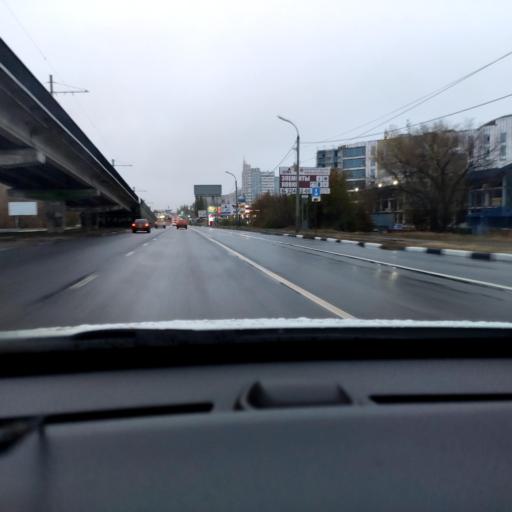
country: RU
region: Voronezj
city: Voronezh
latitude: 51.6889
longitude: 39.2513
